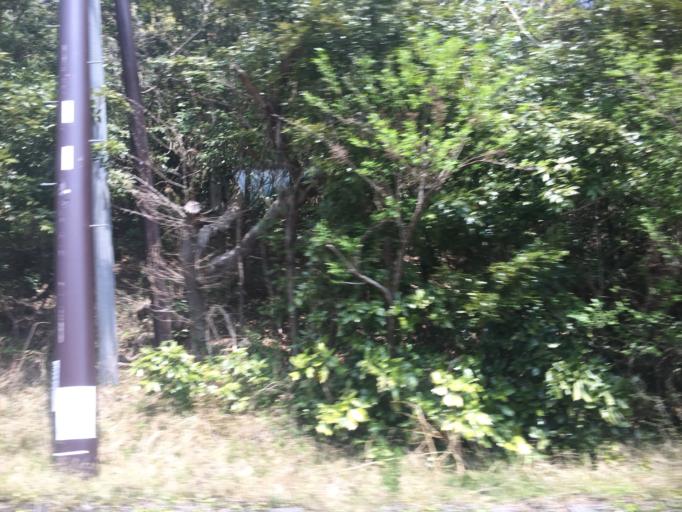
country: JP
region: Shizuoka
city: Ito
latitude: 34.8996
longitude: 139.0920
